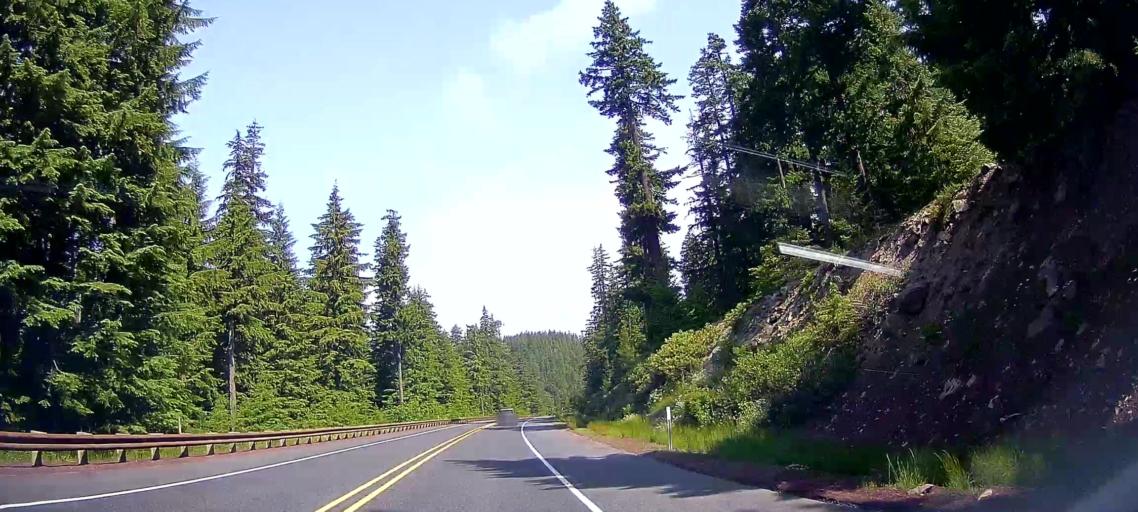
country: US
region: Oregon
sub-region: Clackamas County
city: Mount Hood Village
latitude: 45.2046
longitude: -121.6955
